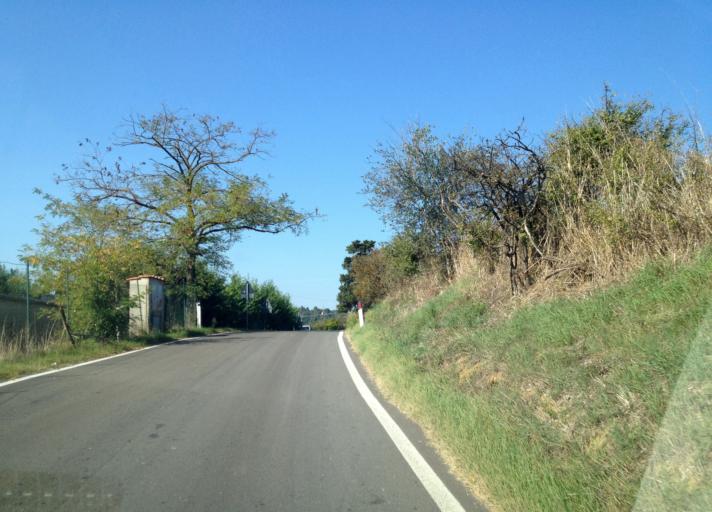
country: IT
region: Tuscany
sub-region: Provincia di Siena
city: Poggibonsi
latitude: 43.4879
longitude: 11.1589
